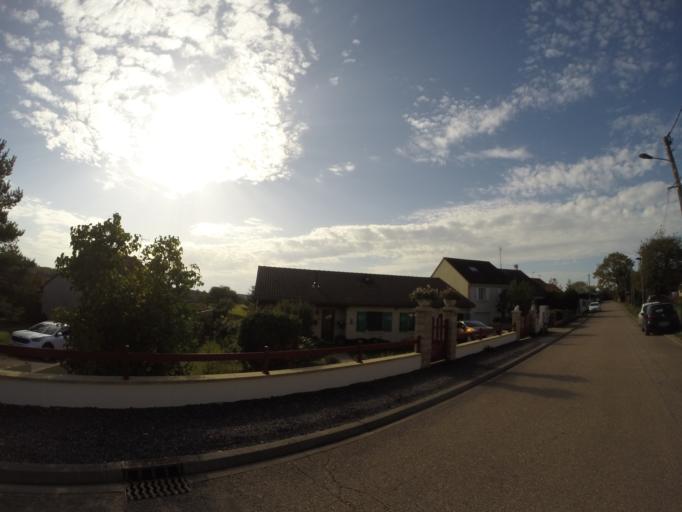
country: FR
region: Lorraine
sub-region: Departement de Meurthe-et-Moselle
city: Colombey-les-Belles
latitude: 48.5220
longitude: 5.8952
